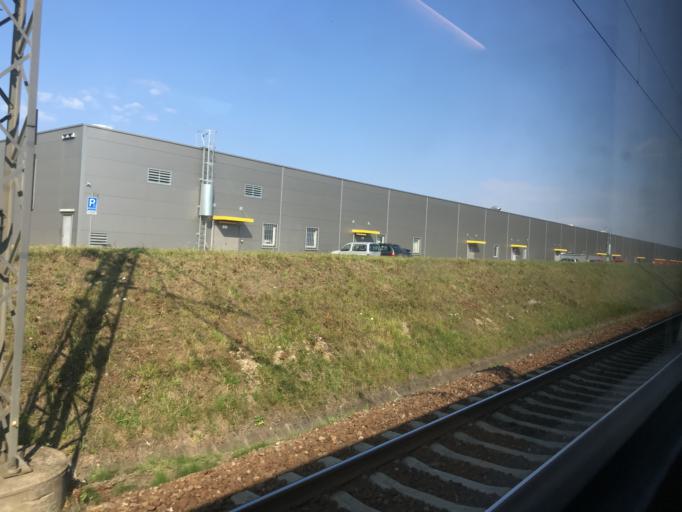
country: CZ
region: Jihocesky
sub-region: Okres Tabor
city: Sezimovo Usti
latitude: 49.3949
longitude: 14.6910
